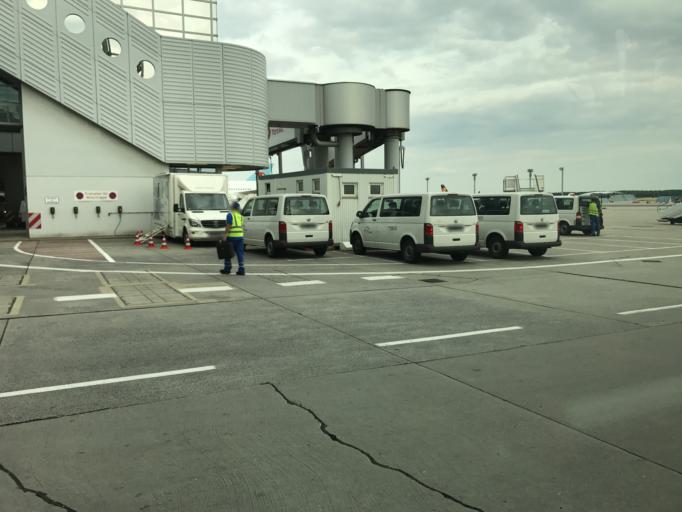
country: DE
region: Hesse
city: Morfelden-Walldorf
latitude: 50.0500
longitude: 8.5836
